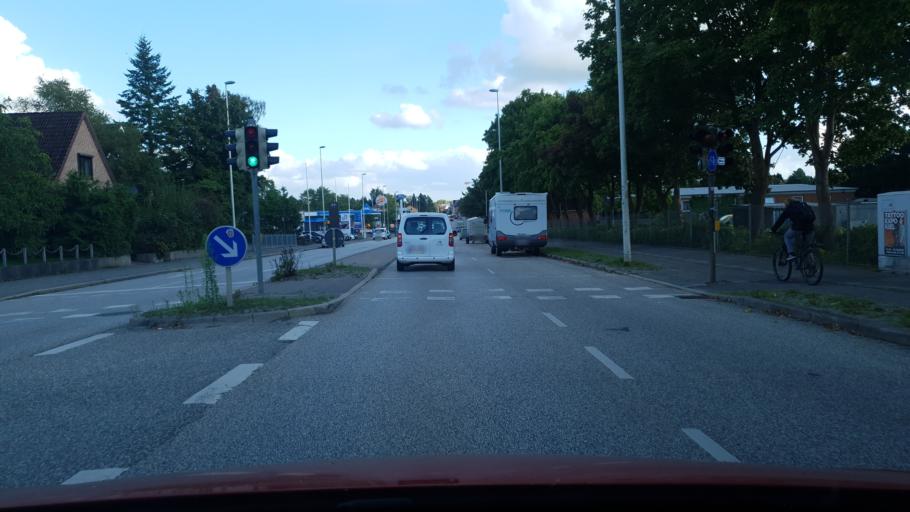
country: DE
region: Schleswig-Holstein
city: Kronshagen
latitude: 54.3473
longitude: 10.0949
